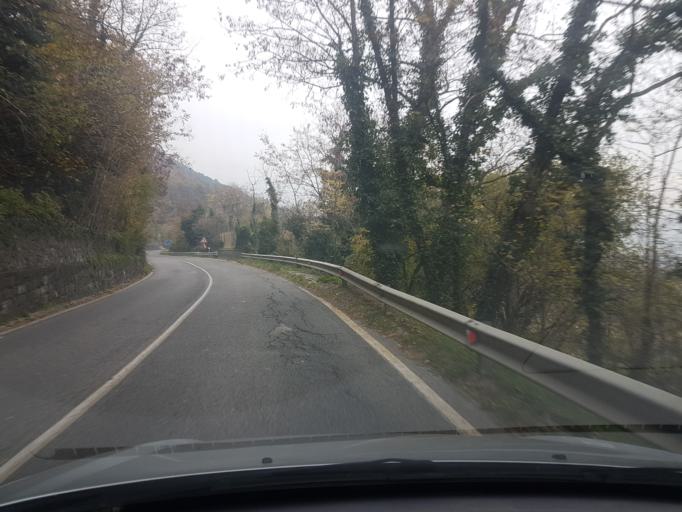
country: IT
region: Friuli Venezia Giulia
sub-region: Provincia di Trieste
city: Domio
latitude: 45.6315
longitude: 13.8415
